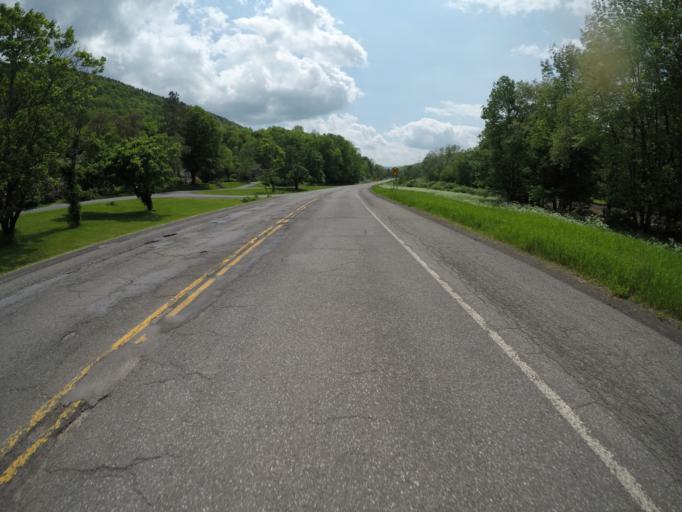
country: US
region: New York
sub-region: Delaware County
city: Stamford
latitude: 42.1804
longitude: -74.6005
